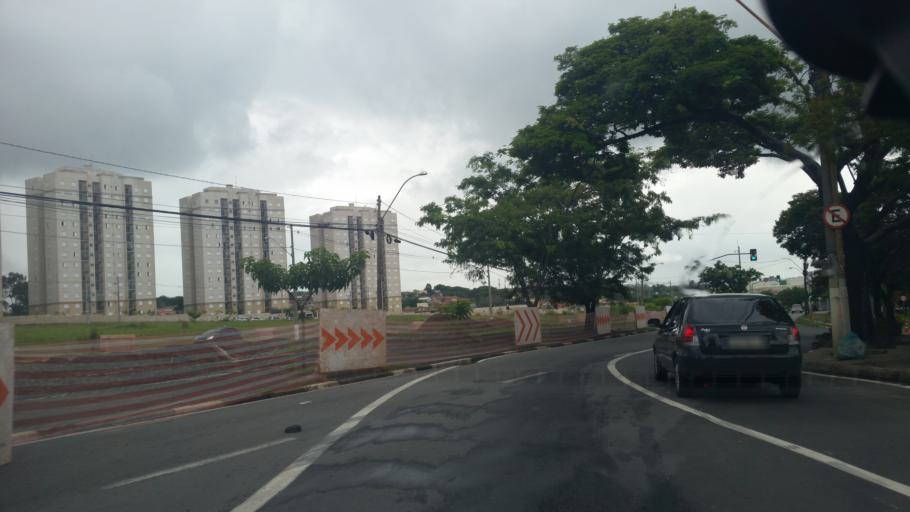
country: BR
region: Sao Paulo
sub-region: Campinas
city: Campinas
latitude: -22.9220
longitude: -47.1185
